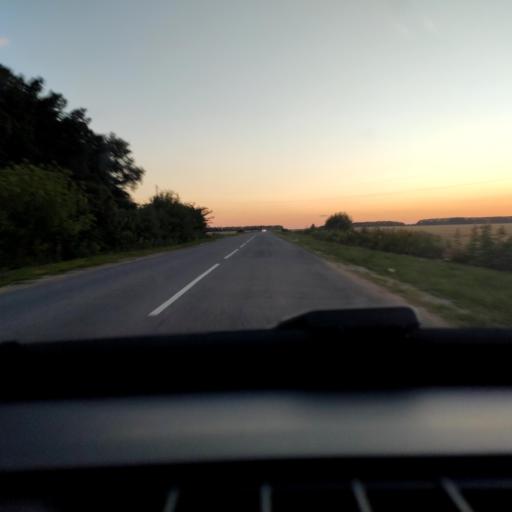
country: RU
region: Lipetsk
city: Zadonsk
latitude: 52.2969
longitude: 38.8268
